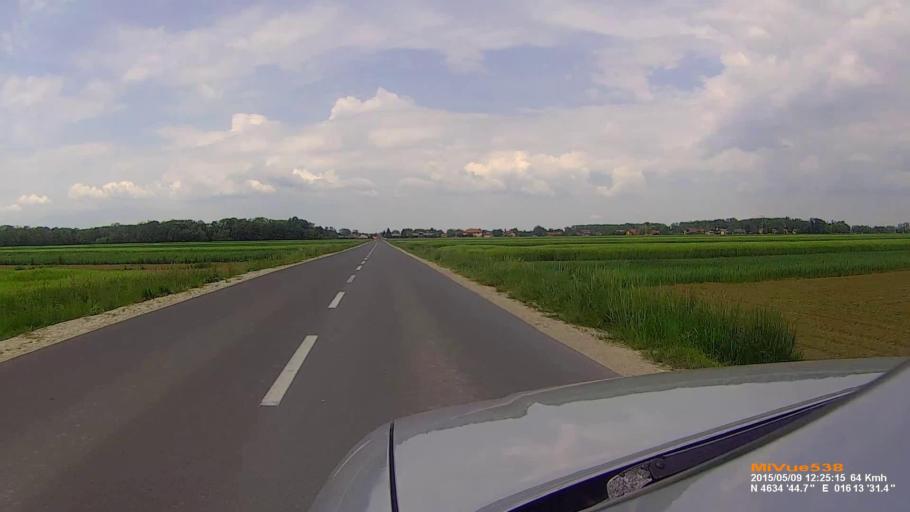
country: SI
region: Beltinci
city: Beltinci
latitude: 46.5790
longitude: 16.2258
